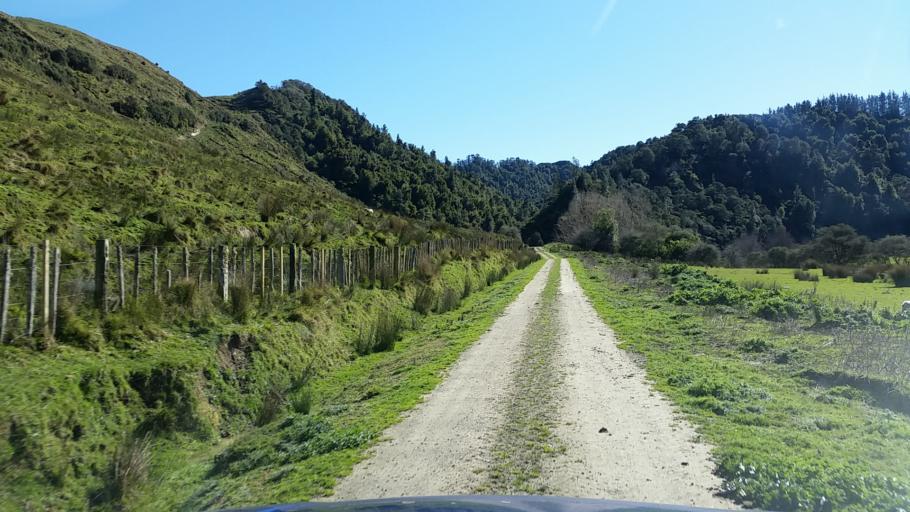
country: NZ
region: Manawatu-Wanganui
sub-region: Wanganui District
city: Wanganui
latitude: -39.6706
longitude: 174.8590
